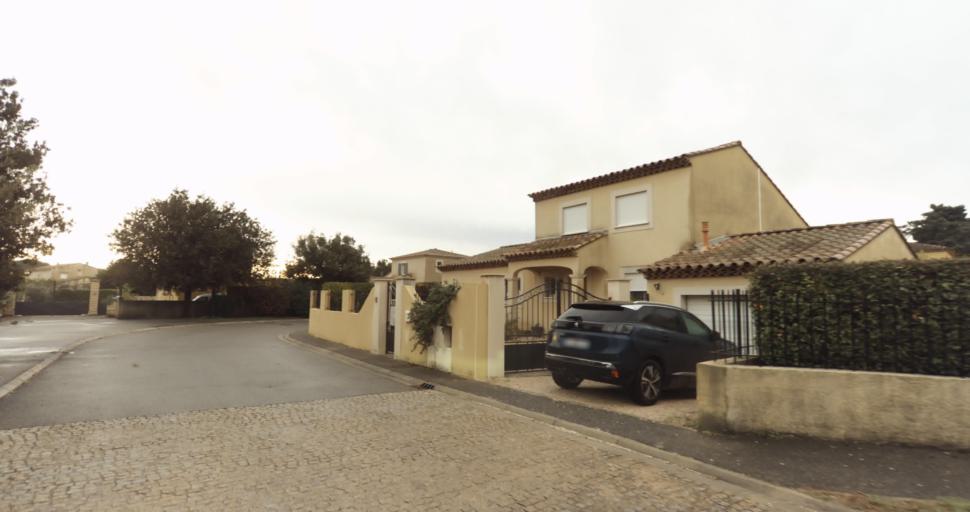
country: FR
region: Provence-Alpes-Cote d'Azur
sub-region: Departement des Bouches-du-Rhone
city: Rognonas
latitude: 43.9042
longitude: 4.8004
